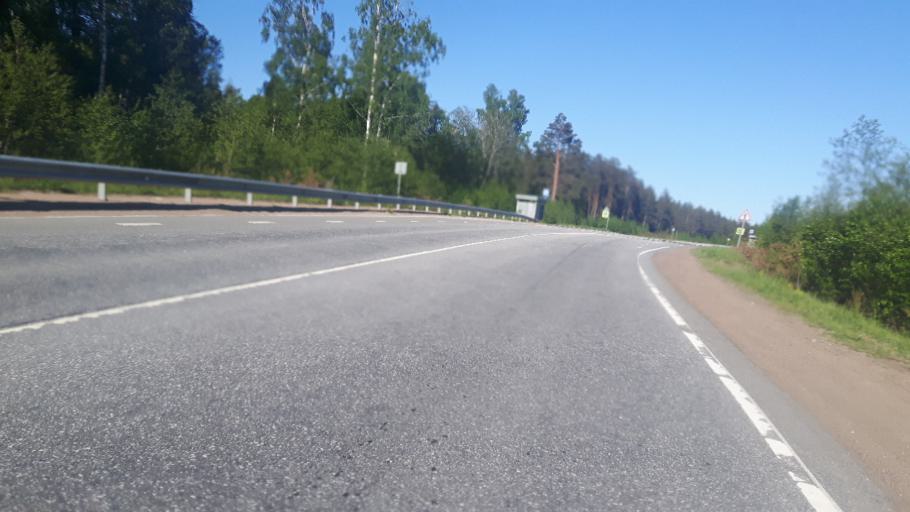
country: RU
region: Leningrad
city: Sosnovyy Bor
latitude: 60.1695
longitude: 29.1896
